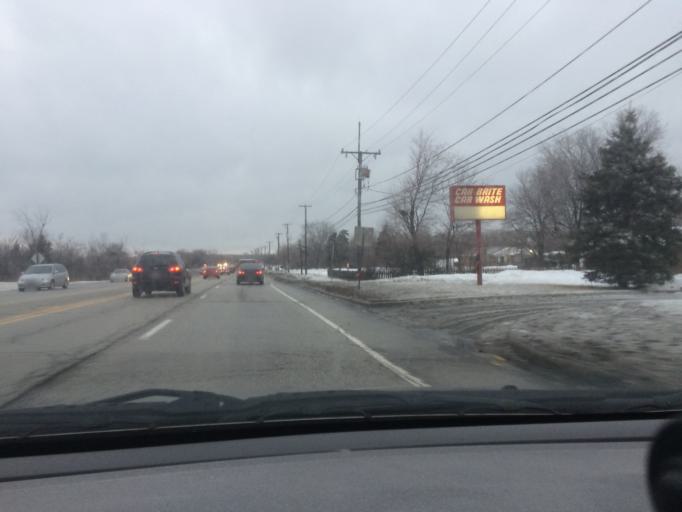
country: US
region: Illinois
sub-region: Cook County
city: Bartlett
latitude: 41.9962
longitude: -88.1670
